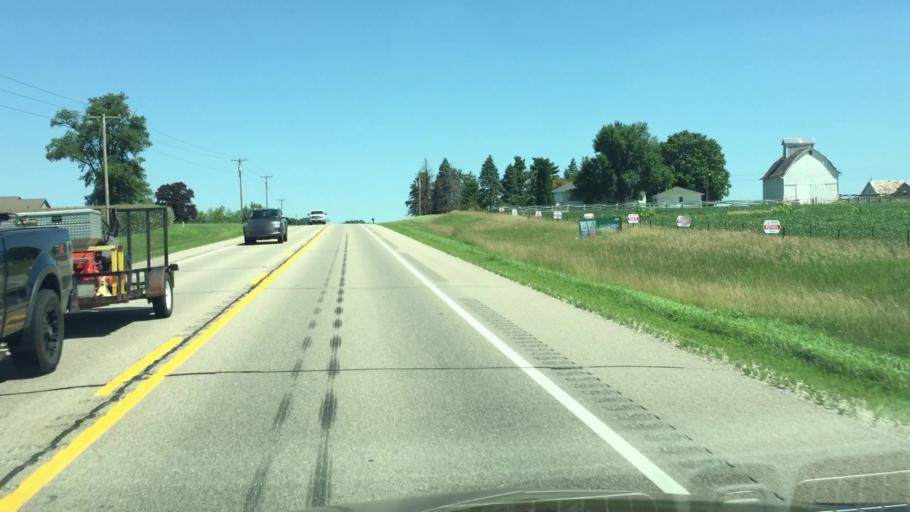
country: US
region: Iowa
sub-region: Johnson County
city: Solon
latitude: 41.8207
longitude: -91.4966
